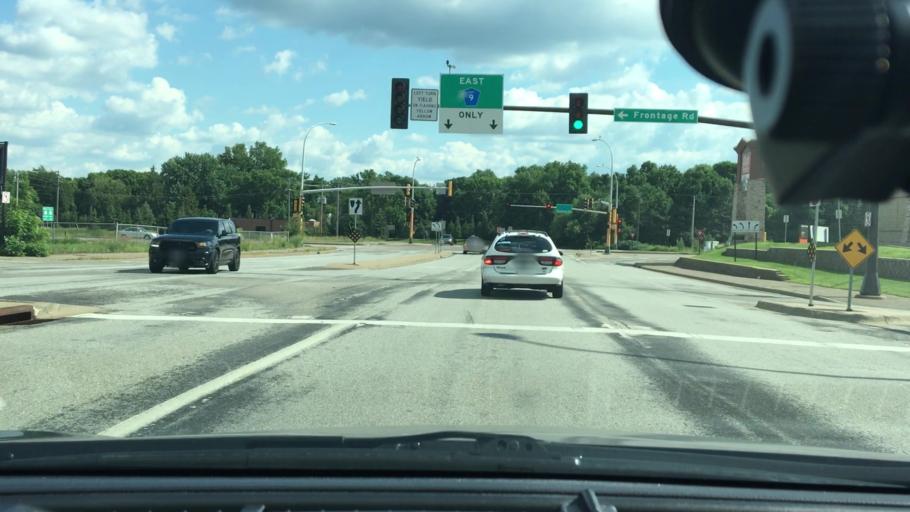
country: US
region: Minnesota
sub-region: Hennepin County
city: New Hope
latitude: 45.0342
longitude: -93.4084
